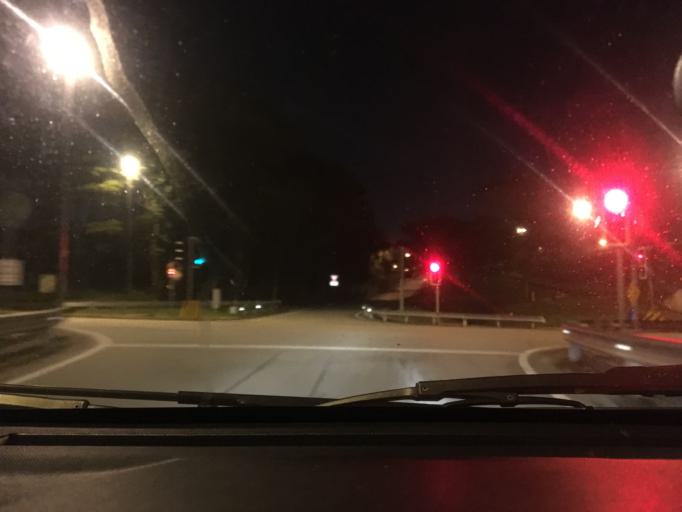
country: MY
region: Selangor
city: Kampong Baharu Balakong
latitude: 2.9871
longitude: 101.7293
